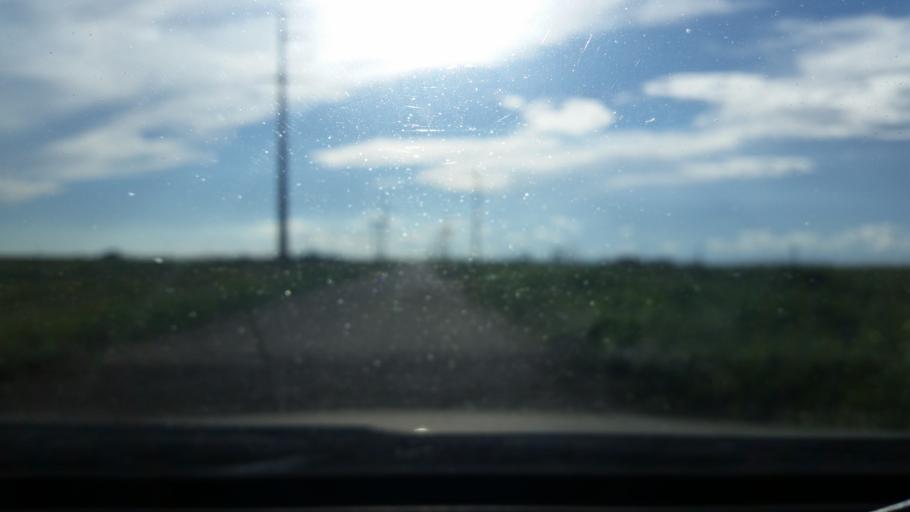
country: US
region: New Mexico
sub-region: Curry County
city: Clovis
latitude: 34.5066
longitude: -103.1921
